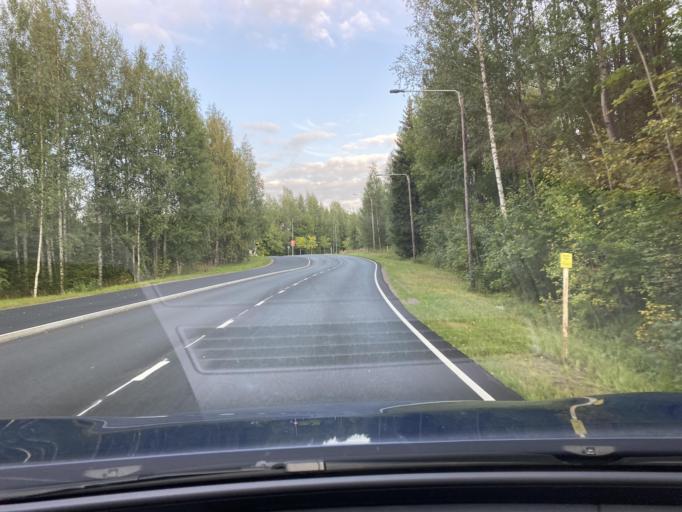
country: FI
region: Kymenlaakso
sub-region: Kouvola
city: Kouvola
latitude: 60.9014
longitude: 26.6464
